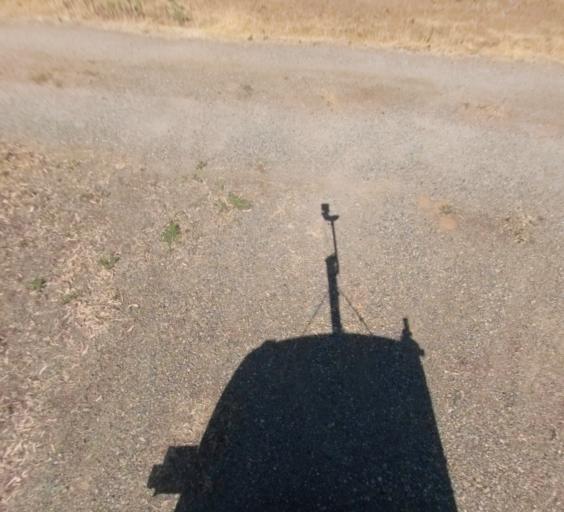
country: US
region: California
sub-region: Madera County
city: Parksdale
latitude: 36.9784
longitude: -120.0173
